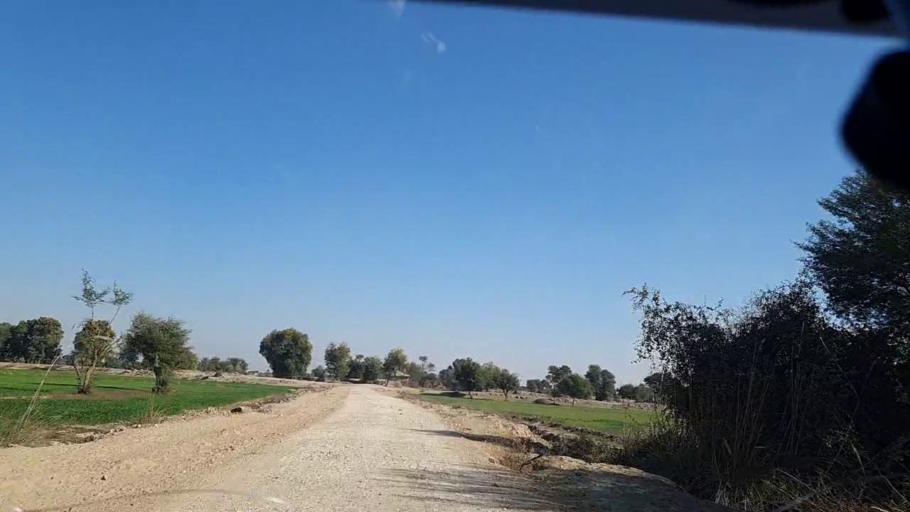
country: PK
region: Sindh
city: Khanpur
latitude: 27.6156
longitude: 69.4483
